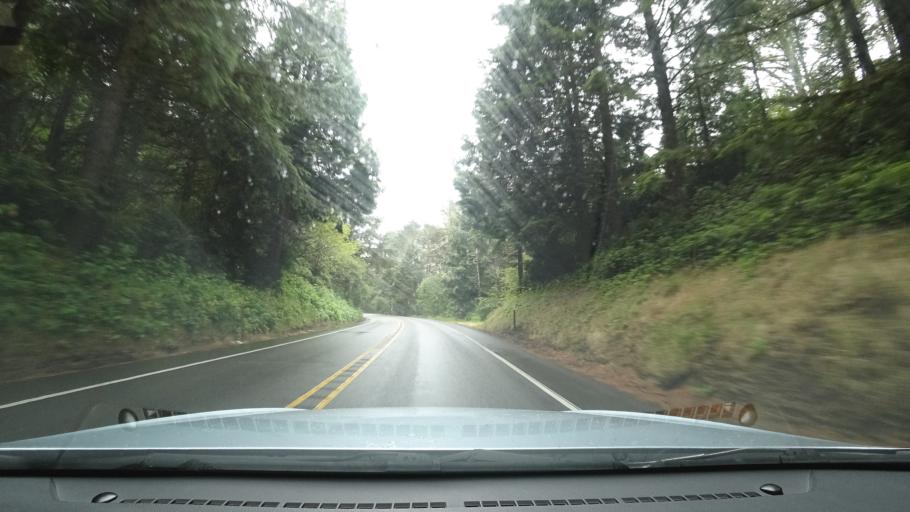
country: US
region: Oregon
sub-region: Lane County
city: Dunes City
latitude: 43.8228
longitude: -124.1485
